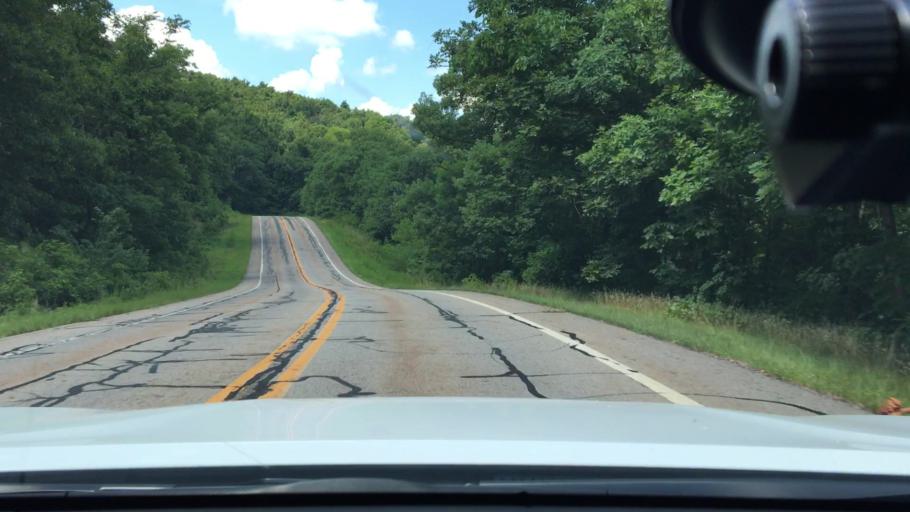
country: US
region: Arkansas
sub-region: Logan County
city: Paris
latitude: 35.1738
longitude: -93.6248
